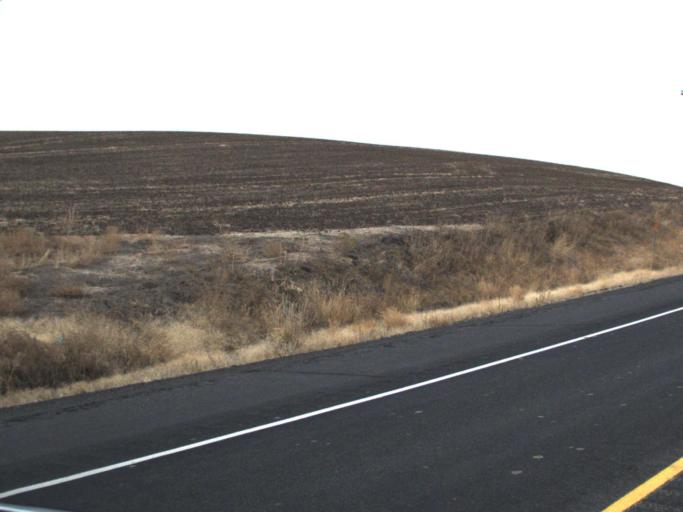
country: US
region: Washington
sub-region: Asotin County
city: Clarkston
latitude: 46.4798
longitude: -117.0547
